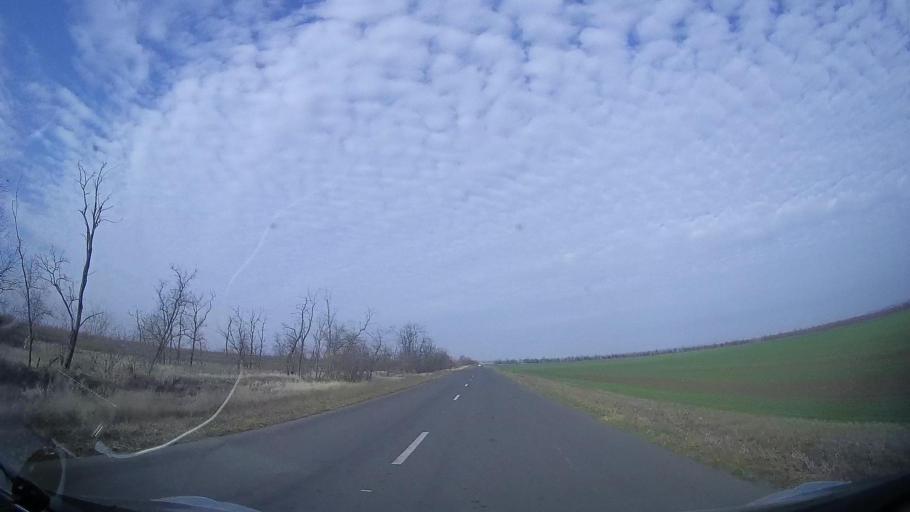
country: RU
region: Rostov
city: Gigant
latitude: 46.8541
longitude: 41.2829
